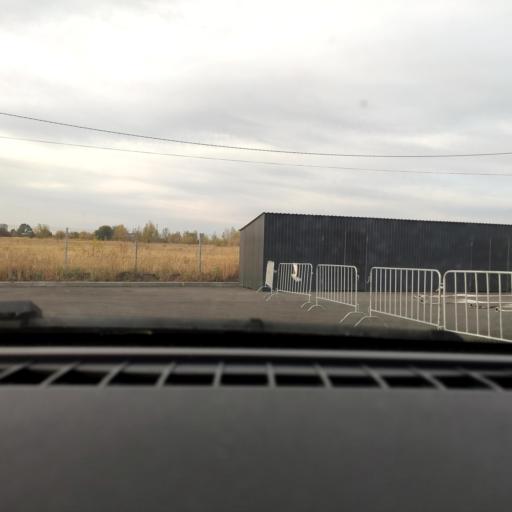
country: RU
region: Voronezj
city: Voronezh
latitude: 51.6780
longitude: 39.2820
